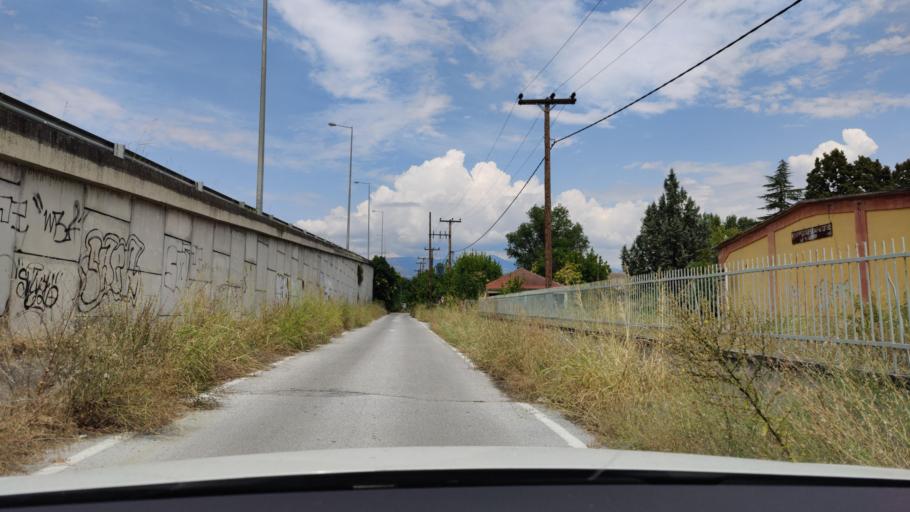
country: GR
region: Central Macedonia
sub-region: Nomos Serron
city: Serres
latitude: 41.0724
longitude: 23.5406
